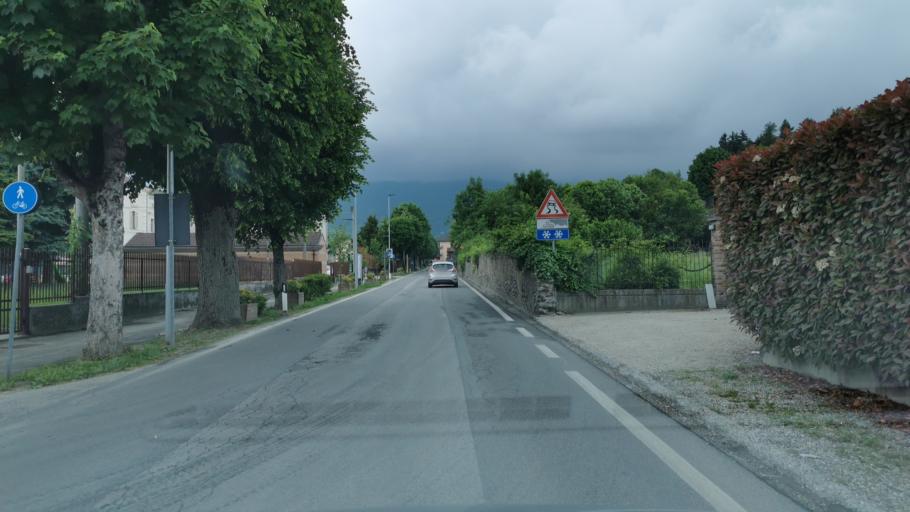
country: IT
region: Piedmont
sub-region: Provincia di Cuneo
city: Caraglio
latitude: 44.4158
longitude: 7.4248
